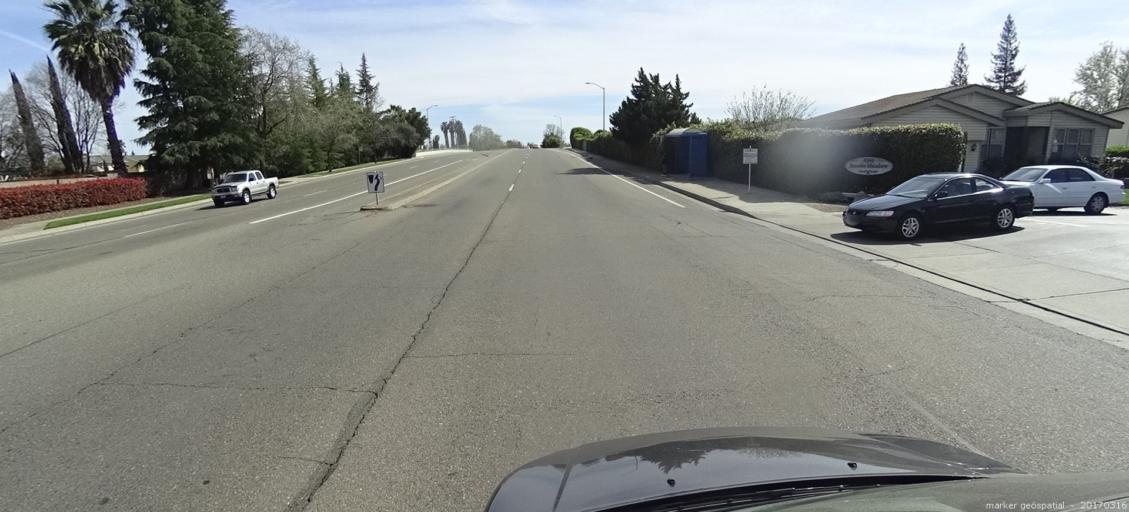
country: US
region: California
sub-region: Sacramento County
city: Parkway
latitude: 38.4789
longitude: -121.4616
